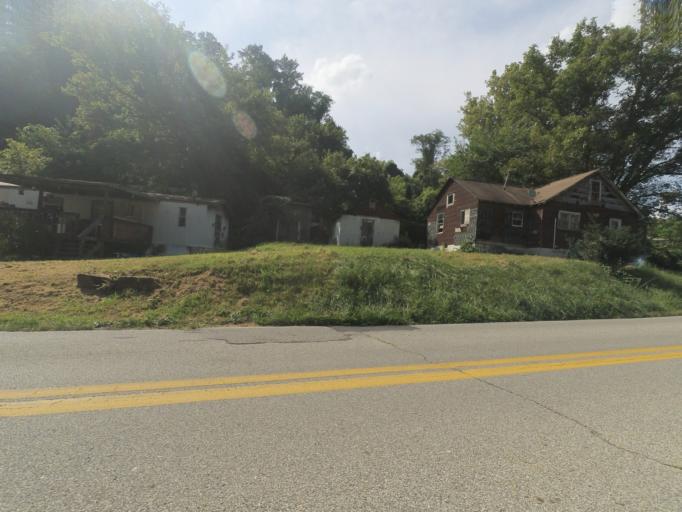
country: US
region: West Virginia
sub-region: Wayne County
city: Ceredo
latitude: 38.3889
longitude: -82.5591
